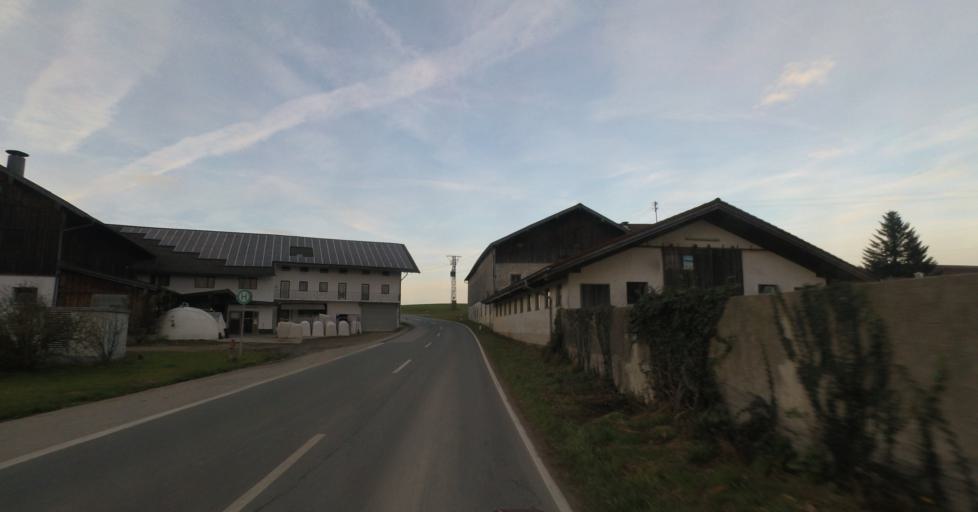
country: DE
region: Bavaria
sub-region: Upper Bavaria
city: Eggstatt
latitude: 47.9050
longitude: 12.3914
